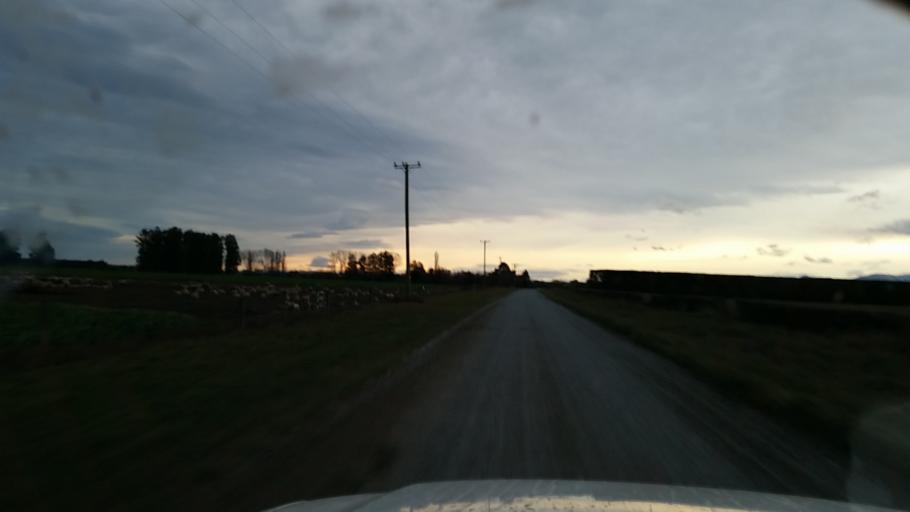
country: NZ
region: Canterbury
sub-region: Ashburton District
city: Ashburton
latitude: -43.8291
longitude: 171.6330
